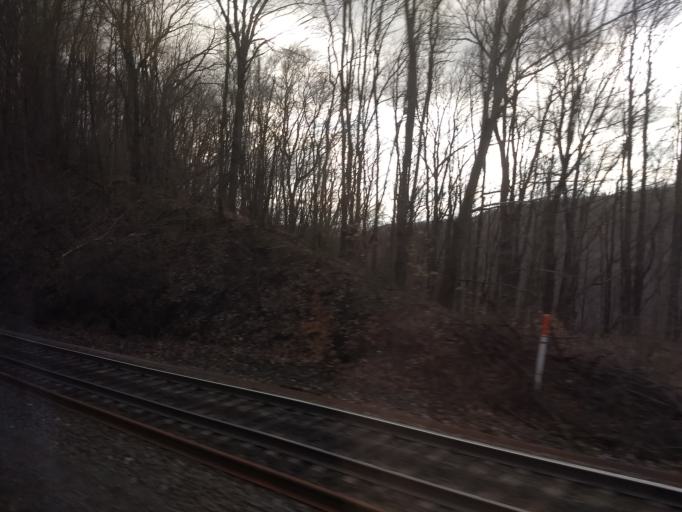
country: US
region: Pennsylvania
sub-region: Cambria County
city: Portage
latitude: 40.4036
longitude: -78.6455
